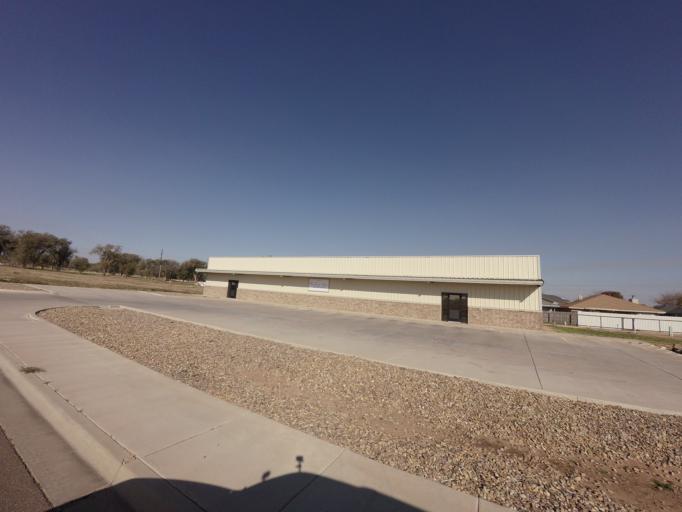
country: US
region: New Mexico
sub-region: Curry County
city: Clovis
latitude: 34.4049
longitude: -103.1774
